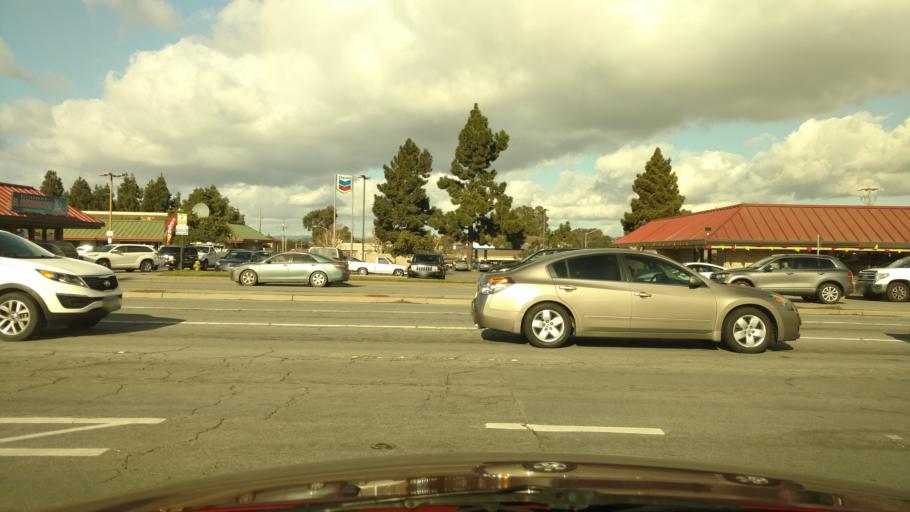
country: US
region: California
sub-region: Monterey County
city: Boronda
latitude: 36.7215
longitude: -121.6570
